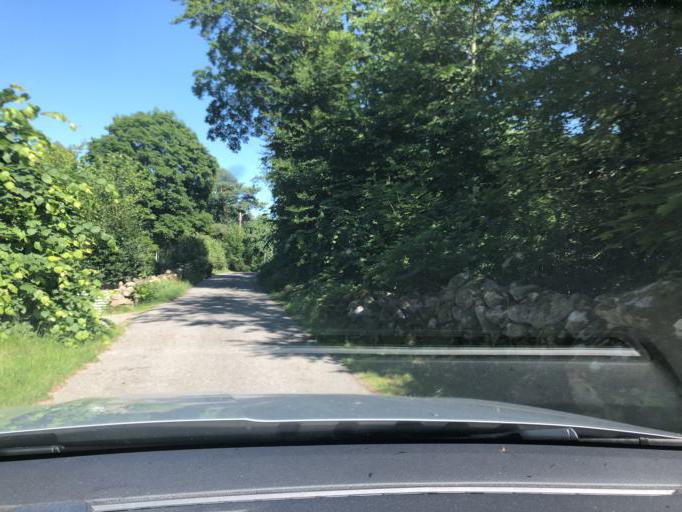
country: SE
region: Blekinge
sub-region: Karlshamns Kommun
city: Morrum
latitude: 56.1902
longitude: 14.6851
